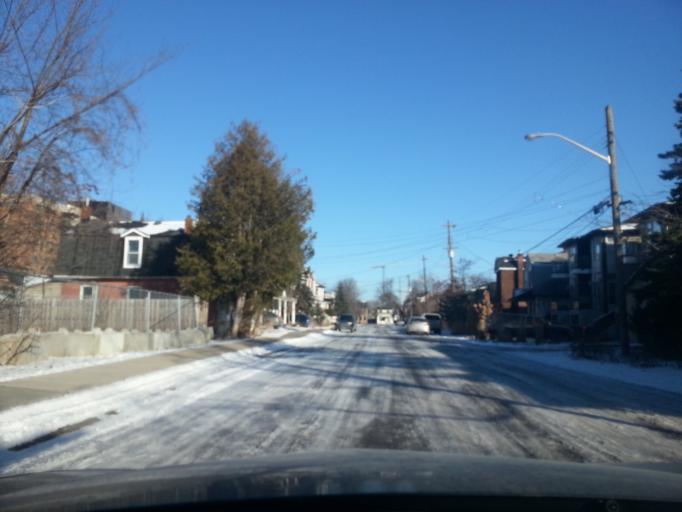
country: CA
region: Ontario
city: Ottawa
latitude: 45.3931
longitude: -75.7574
